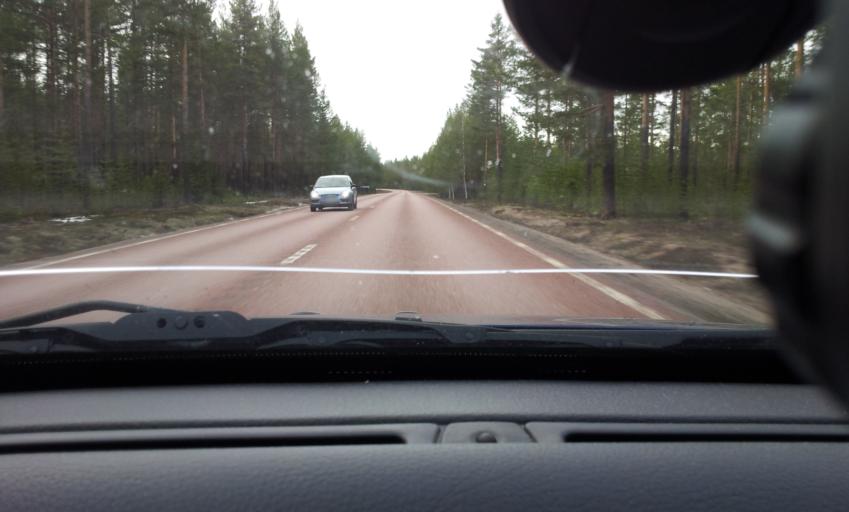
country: SE
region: Gaevleborg
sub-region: Ljusdals Kommun
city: Farila
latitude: 61.9097
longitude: 15.6290
